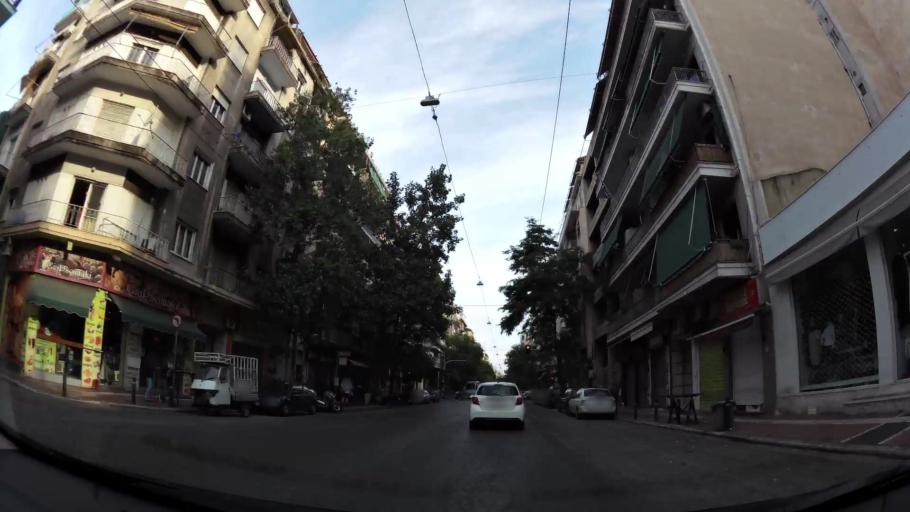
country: GR
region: Attica
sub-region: Nomarchia Athinas
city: Kipseli
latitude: 37.9914
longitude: 23.7269
